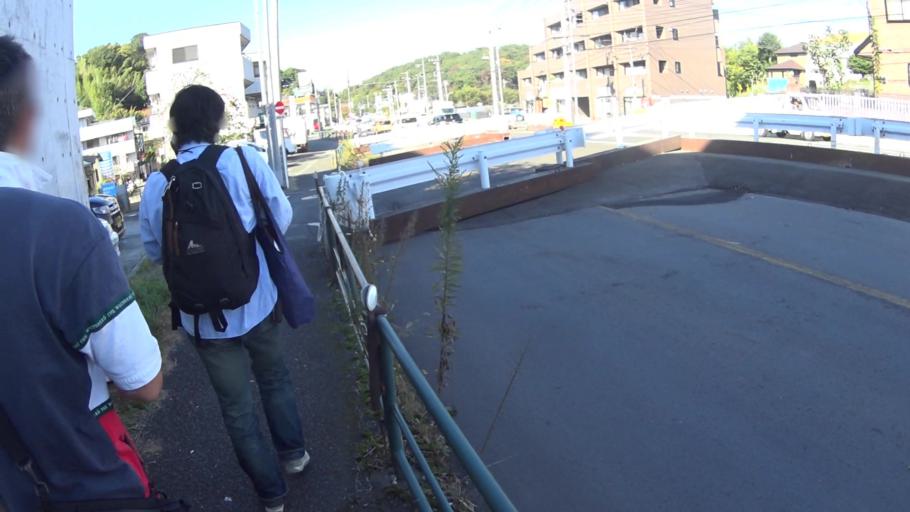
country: JP
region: Tokyo
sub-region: Machida-shi
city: Machida
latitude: 35.5634
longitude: 139.4446
